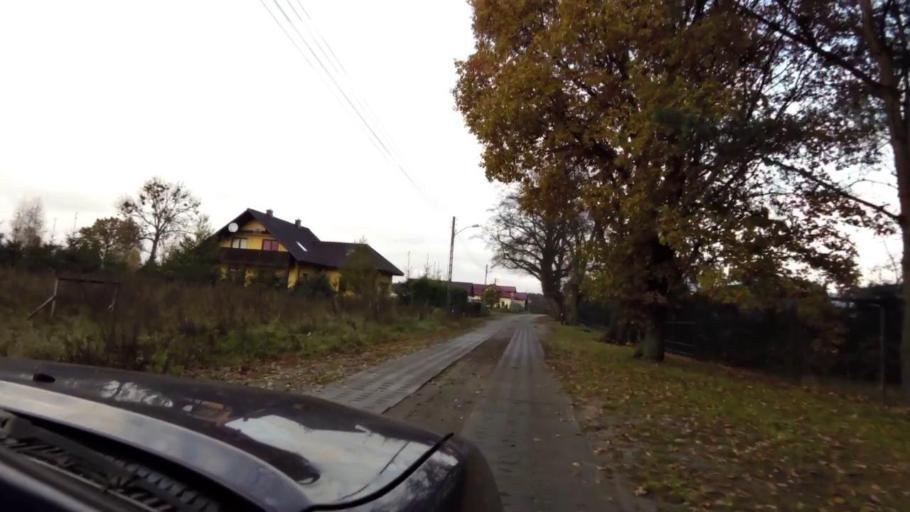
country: PL
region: West Pomeranian Voivodeship
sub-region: Powiat goleniowski
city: Goleniow
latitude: 53.5861
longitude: 14.7622
